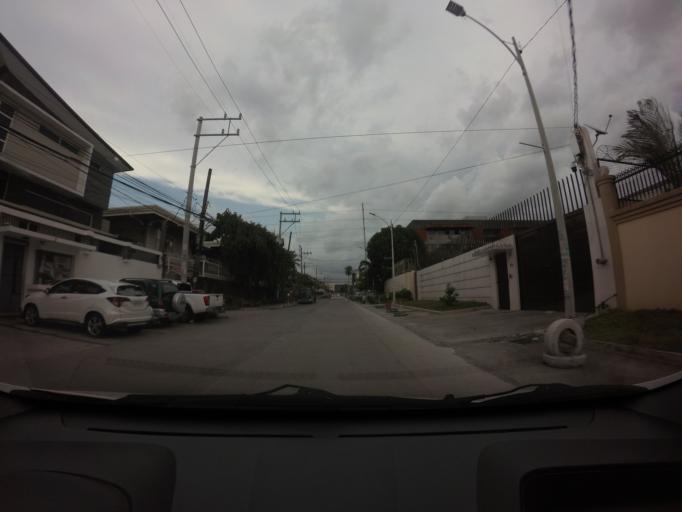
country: PH
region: Calabarzon
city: Del Monte
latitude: 14.6204
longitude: 121.0065
